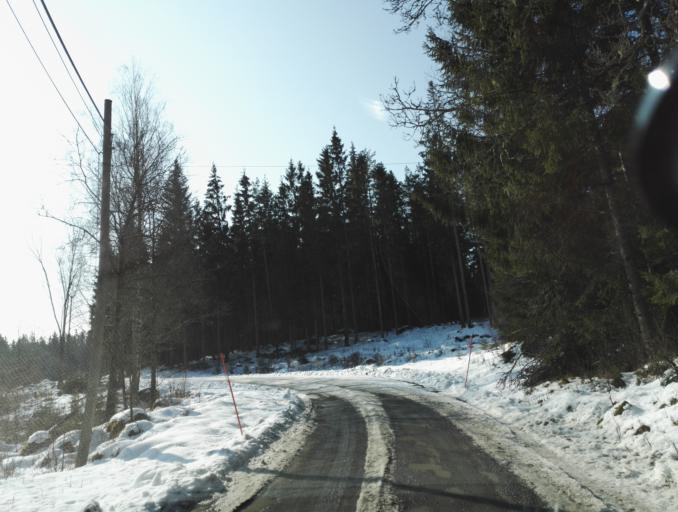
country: SE
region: Vaestra Goetaland
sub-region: Bollebygds Kommun
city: Bollebygd
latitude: 57.7567
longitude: 12.5919
